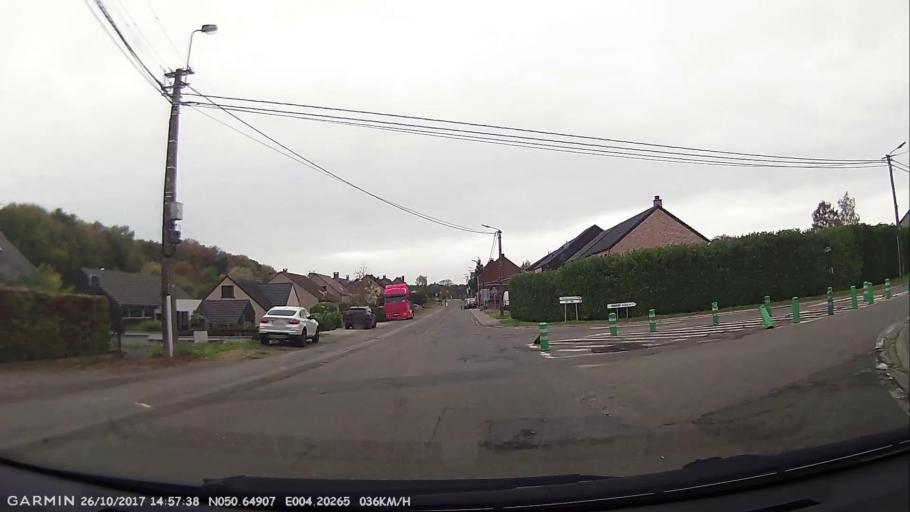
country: BE
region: Wallonia
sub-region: Province du Brabant Wallon
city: Tubize
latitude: 50.6490
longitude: 4.2027
